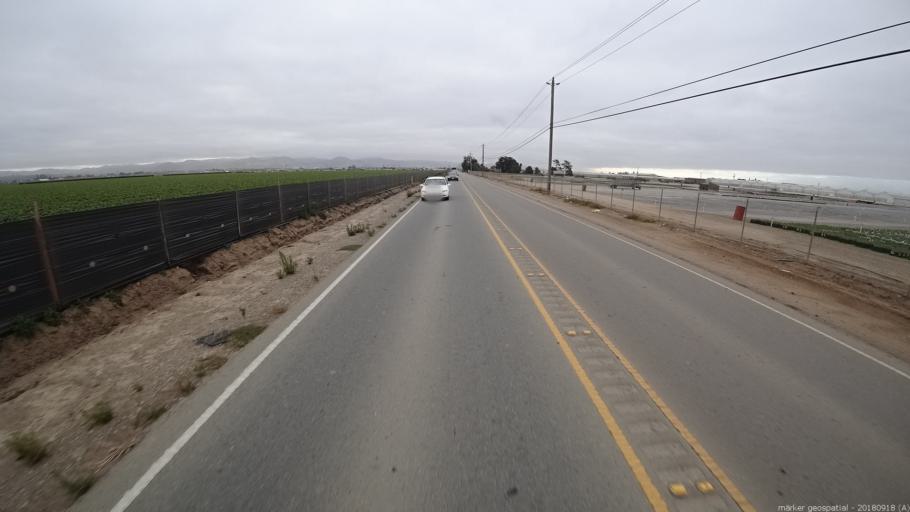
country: US
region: California
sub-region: Monterey County
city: Prunedale
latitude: 36.7412
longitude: -121.6803
